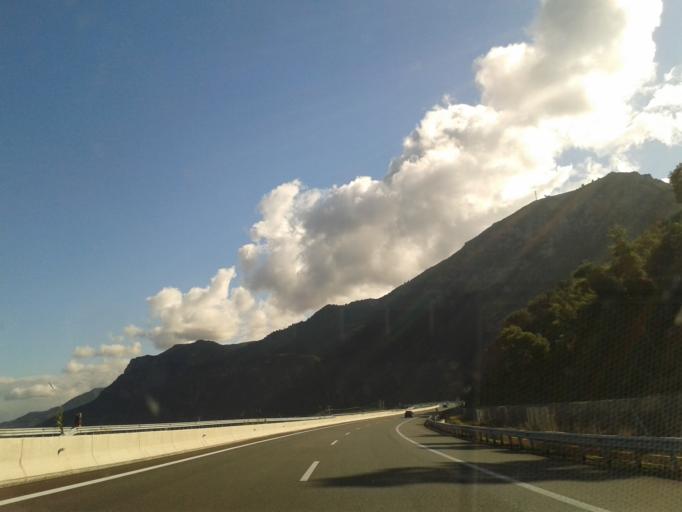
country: GR
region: West Greece
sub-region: Nomos Achaias
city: Temeni
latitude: 38.2006
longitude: 22.1483
